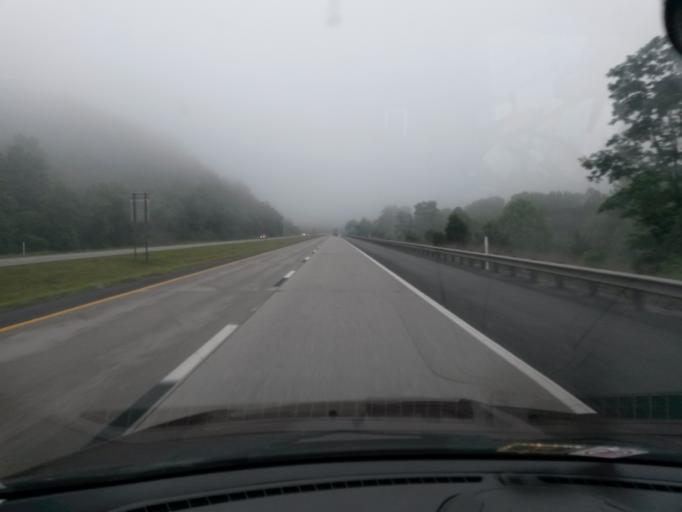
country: US
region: West Virginia
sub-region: Summers County
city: Hinton
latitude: 37.8142
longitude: -80.8141
